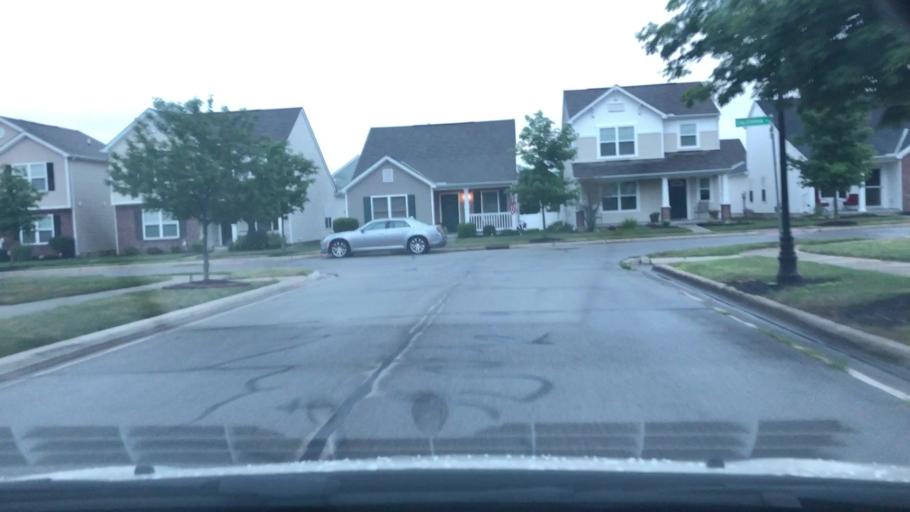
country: US
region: Ohio
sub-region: Franklin County
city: New Albany
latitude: 40.0969
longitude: -82.8541
